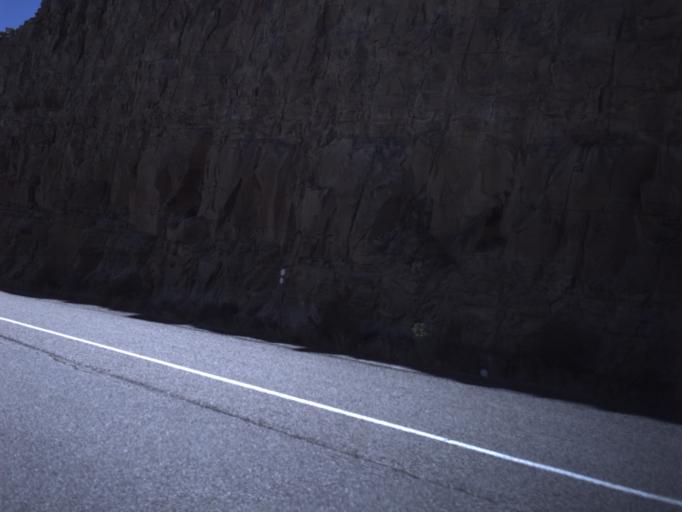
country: US
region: Utah
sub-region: Emery County
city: Ferron
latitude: 38.8301
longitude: -111.1142
